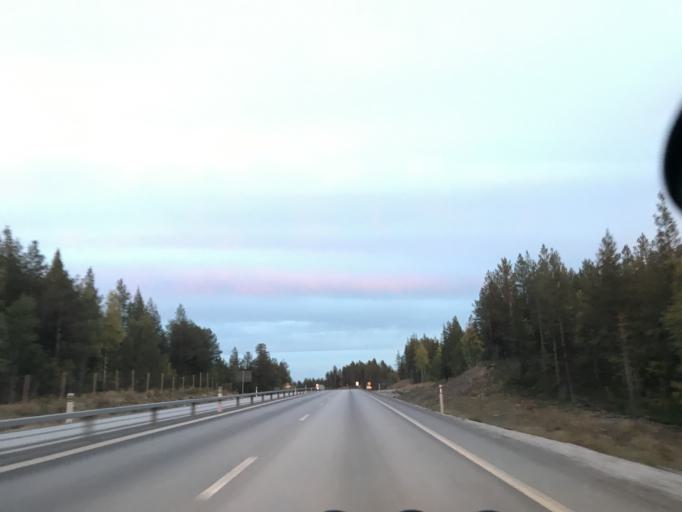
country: SE
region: Norrbotten
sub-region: Gallivare Kommun
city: Malmberget
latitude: 67.6687
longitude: 20.9586
